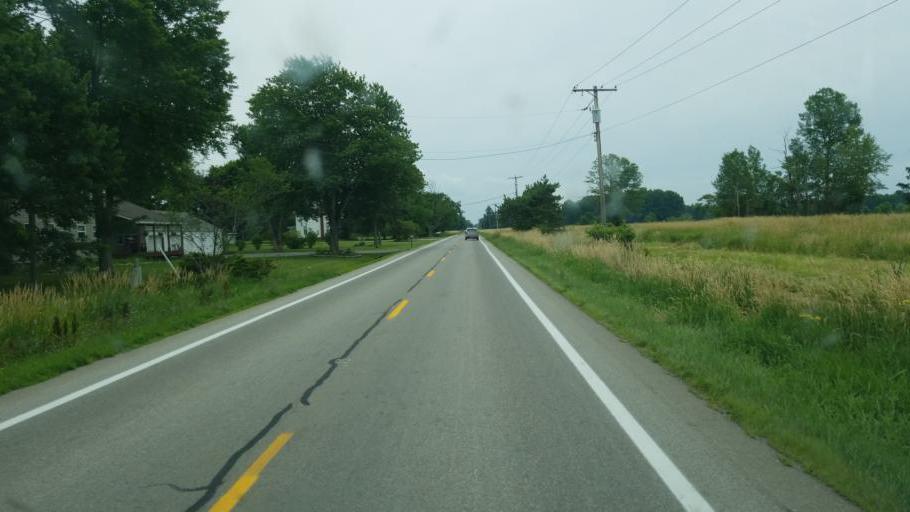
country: US
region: Ohio
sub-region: Ashtabula County
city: Orwell
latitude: 41.4616
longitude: -80.8279
